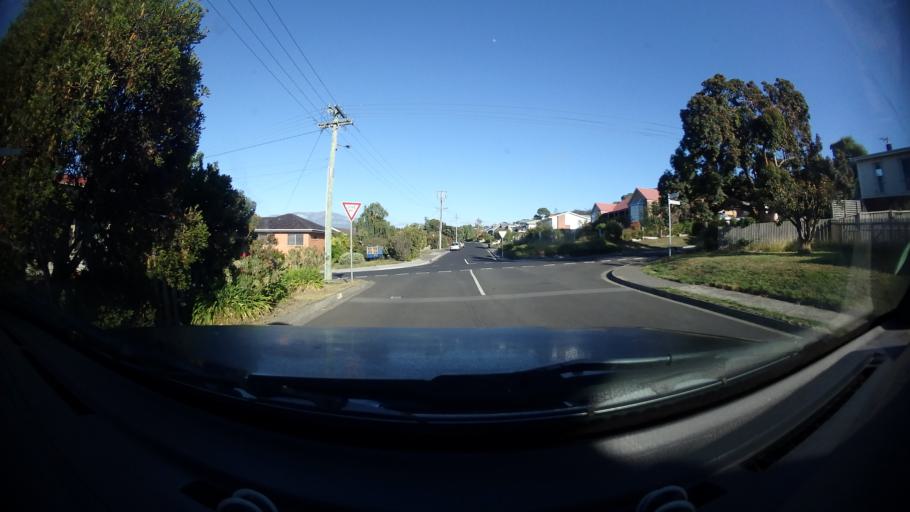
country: AU
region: Tasmania
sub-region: Clarence
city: Howrah
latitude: -42.8750
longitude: 147.3940
